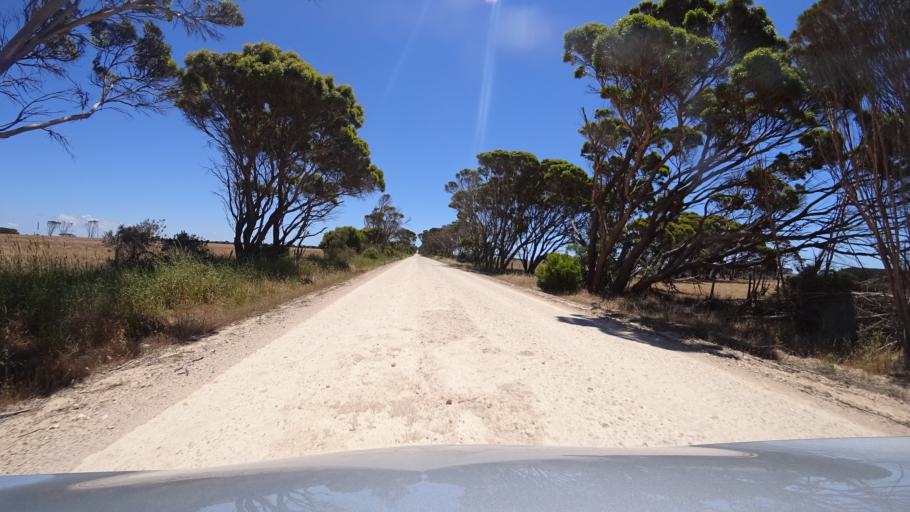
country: AU
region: South Australia
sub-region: Kangaroo Island
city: Kingscote
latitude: -35.7525
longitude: 138.0266
